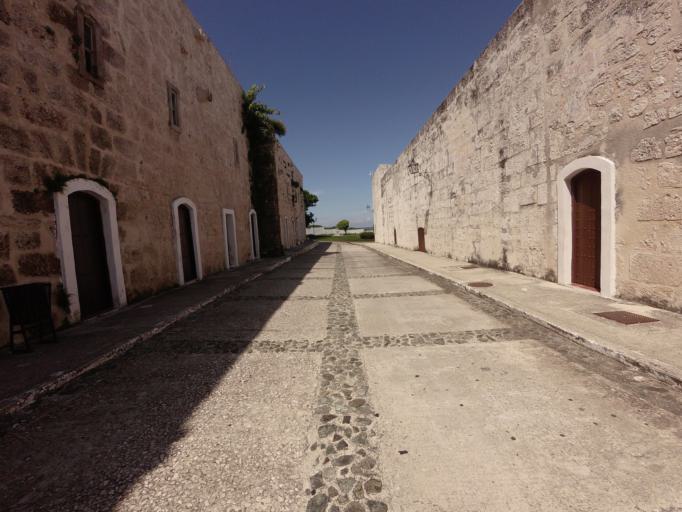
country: CU
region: La Habana
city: Centro Habana
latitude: 23.1474
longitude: -82.3509
